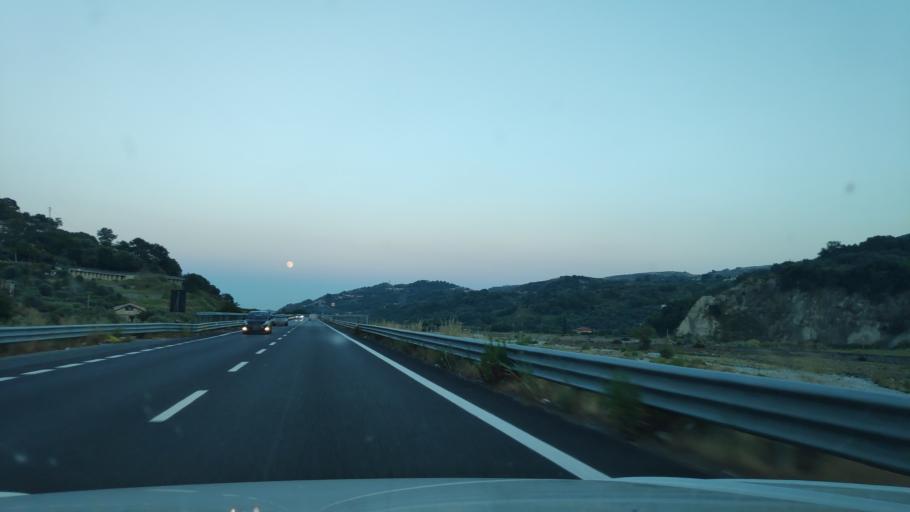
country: IT
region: Calabria
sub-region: Provincia di Reggio Calabria
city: Mammola
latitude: 38.3536
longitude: 16.2448
